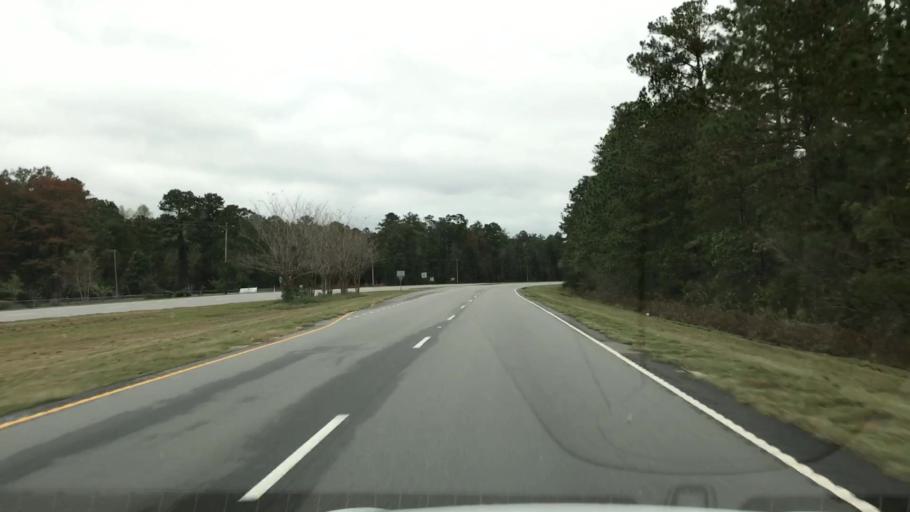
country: US
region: South Carolina
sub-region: Georgetown County
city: Georgetown
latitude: 33.2483
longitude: -79.3751
